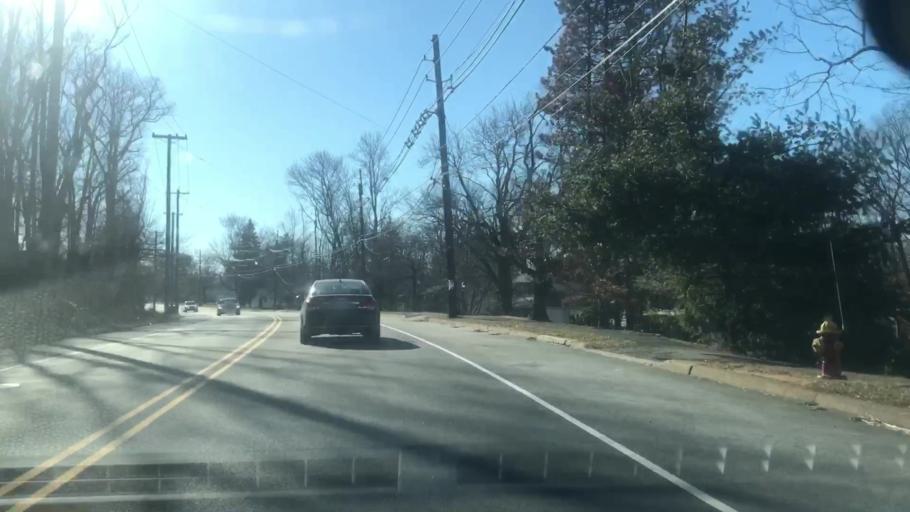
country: US
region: New Jersey
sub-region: Essex County
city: Livingston
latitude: 40.8009
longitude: -74.2963
